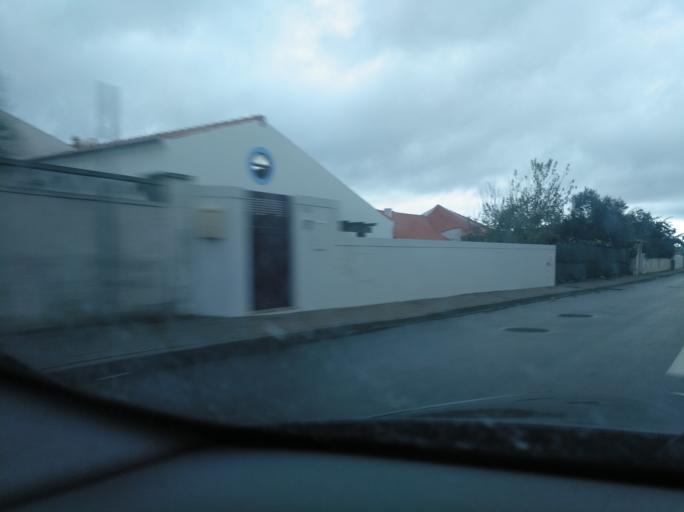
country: PT
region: Beja
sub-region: Aljustrel
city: Aljustrel
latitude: 37.8789
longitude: -8.1560
